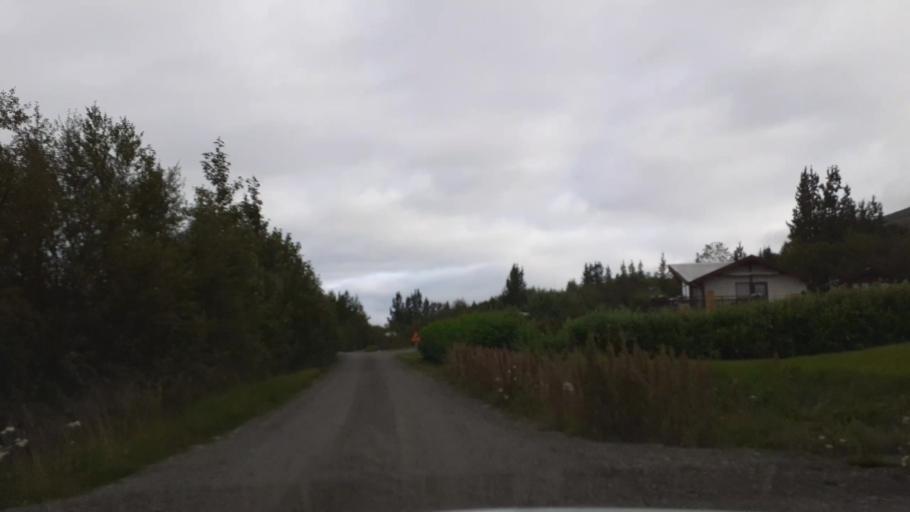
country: IS
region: Northeast
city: Akureyri
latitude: 65.6776
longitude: -18.0413
